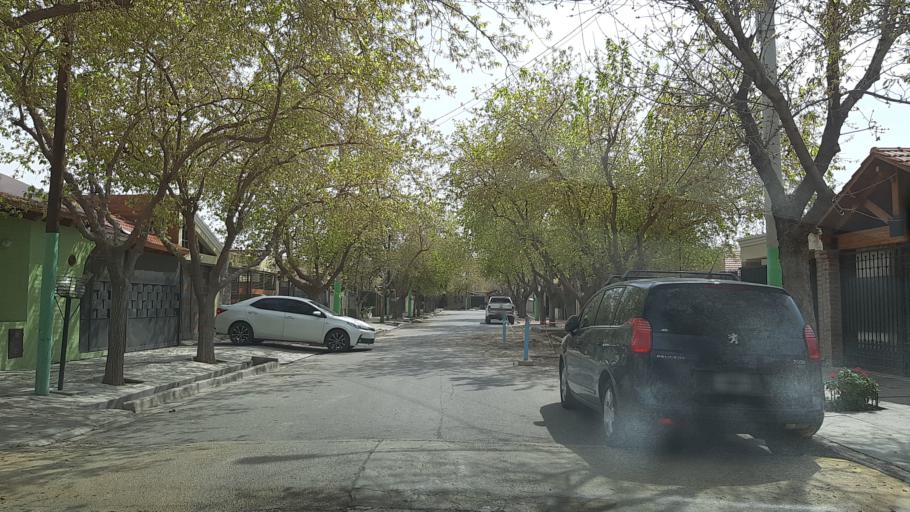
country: AR
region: San Juan
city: San Juan
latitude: -31.5379
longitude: -68.5954
